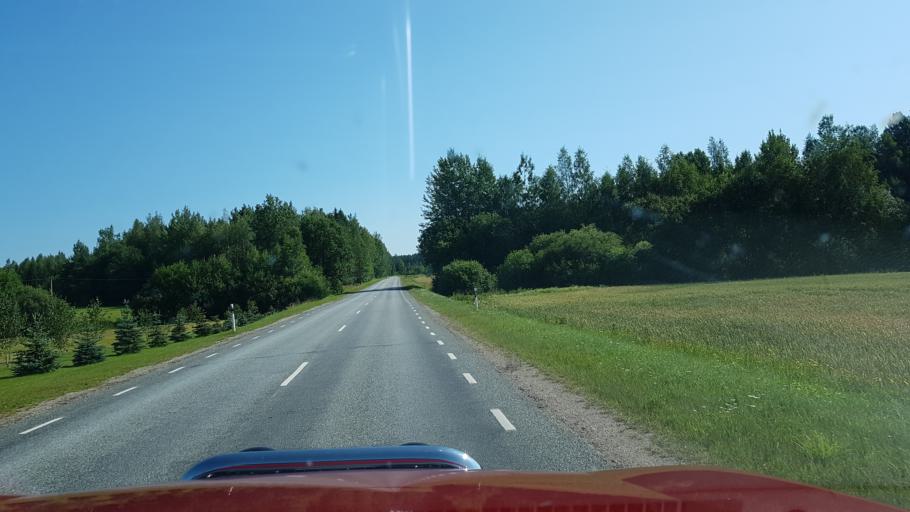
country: EE
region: Polvamaa
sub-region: Polva linn
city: Polva
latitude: 58.0022
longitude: 26.9347
